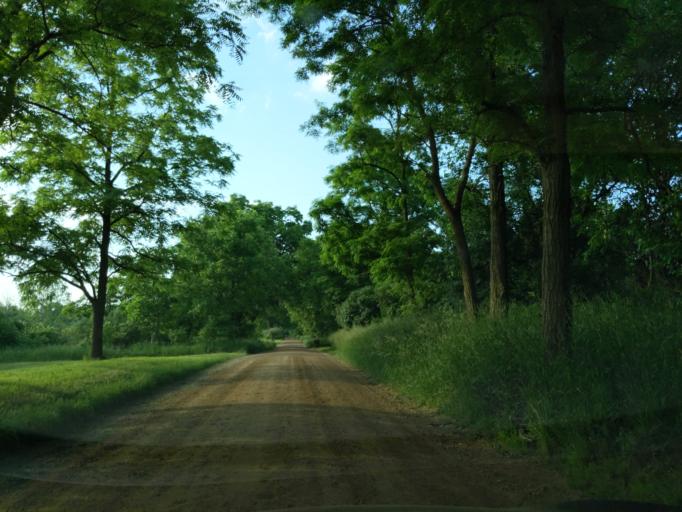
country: US
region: Michigan
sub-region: Shiawassee County
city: Laingsburg
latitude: 42.8488
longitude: -84.3643
